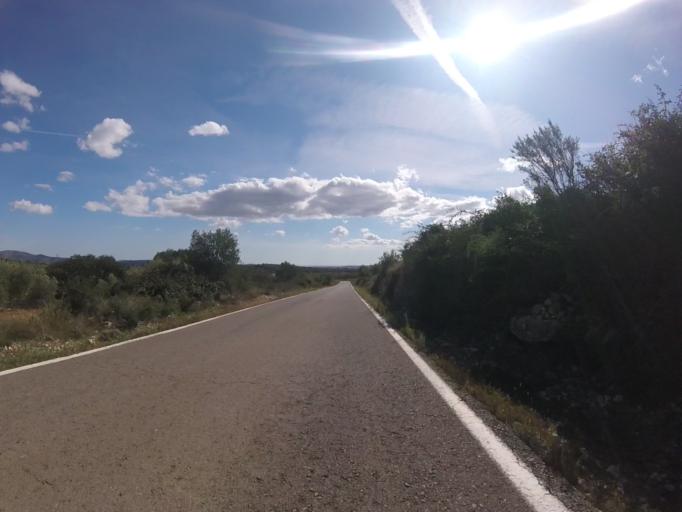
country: ES
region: Valencia
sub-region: Provincia de Castello
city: Albocasser
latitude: 40.4005
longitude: 0.0856
